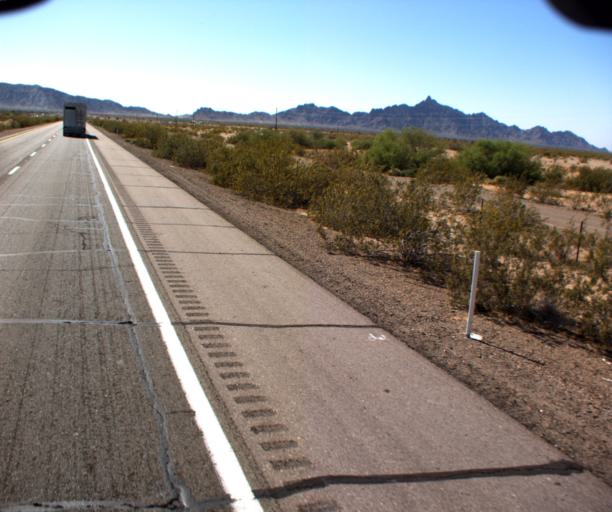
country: US
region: Arizona
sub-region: Yuma County
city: Wellton
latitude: 32.7430
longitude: -113.6829
